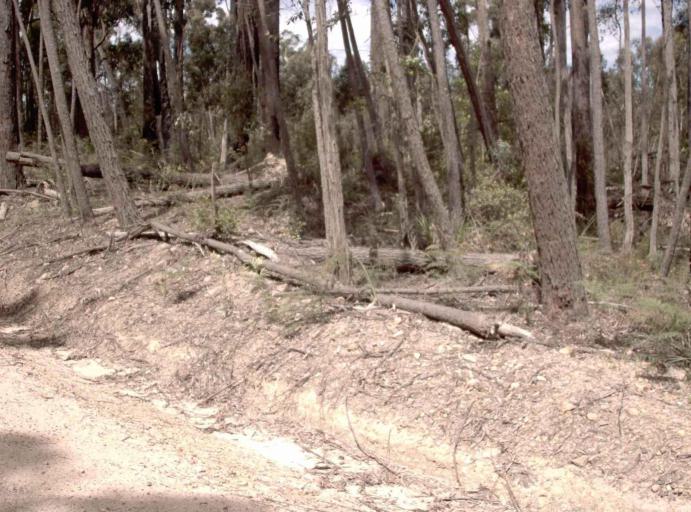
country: AU
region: Victoria
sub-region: East Gippsland
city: Lakes Entrance
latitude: -37.6547
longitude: 148.6516
